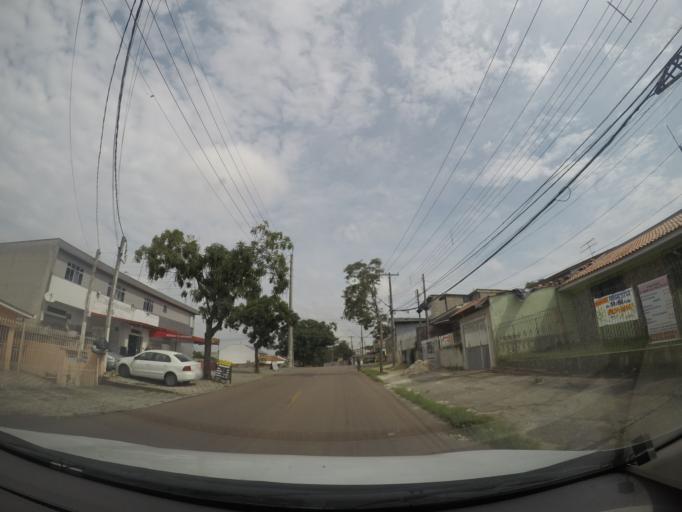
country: BR
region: Parana
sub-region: Sao Jose Dos Pinhais
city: Sao Jose dos Pinhais
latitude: -25.5224
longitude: -49.2837
